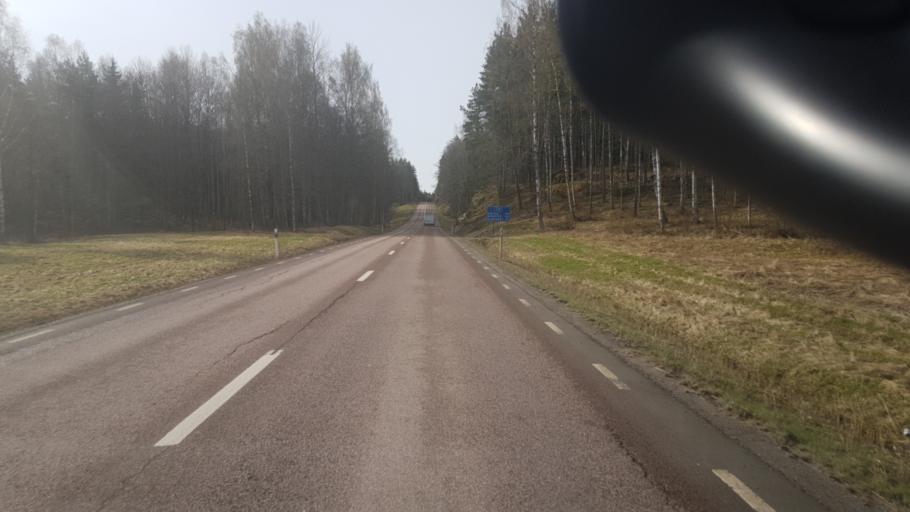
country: SE
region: Vaermland
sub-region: Arvika Kommun
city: Arvika
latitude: 59.6377
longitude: 12.6168
